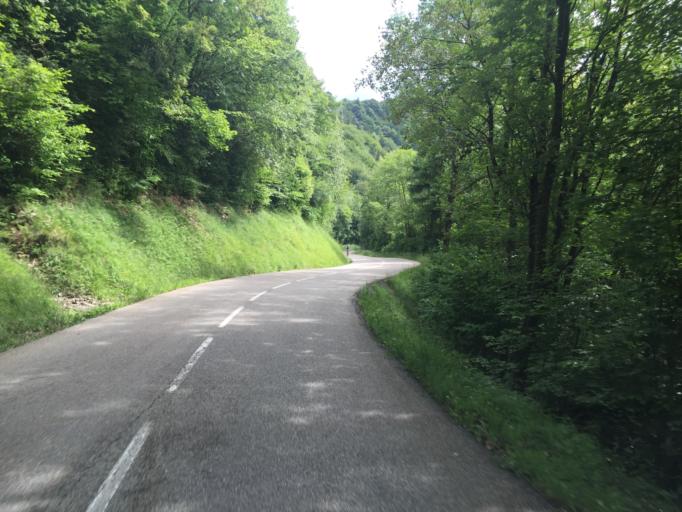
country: FR
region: Rhone-Alpes
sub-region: Departement de la Savoie
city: Saint-Baldoph
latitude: 45.5193
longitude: 5.9257
